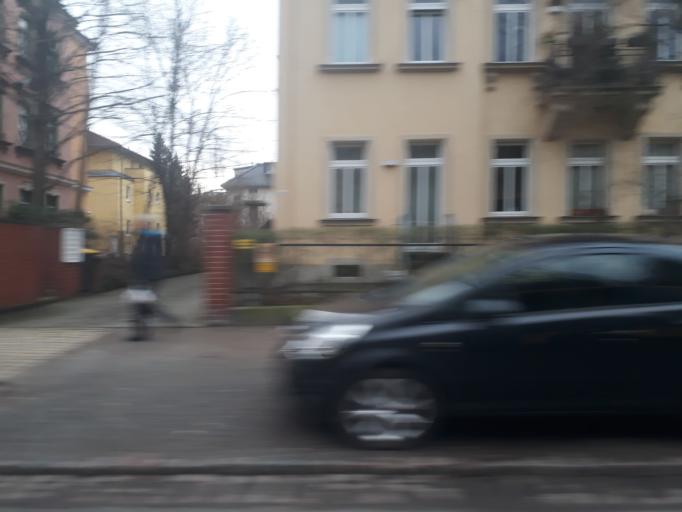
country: DE
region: Saxony
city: Albertstadt
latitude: 51.0486
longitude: 13.8001
